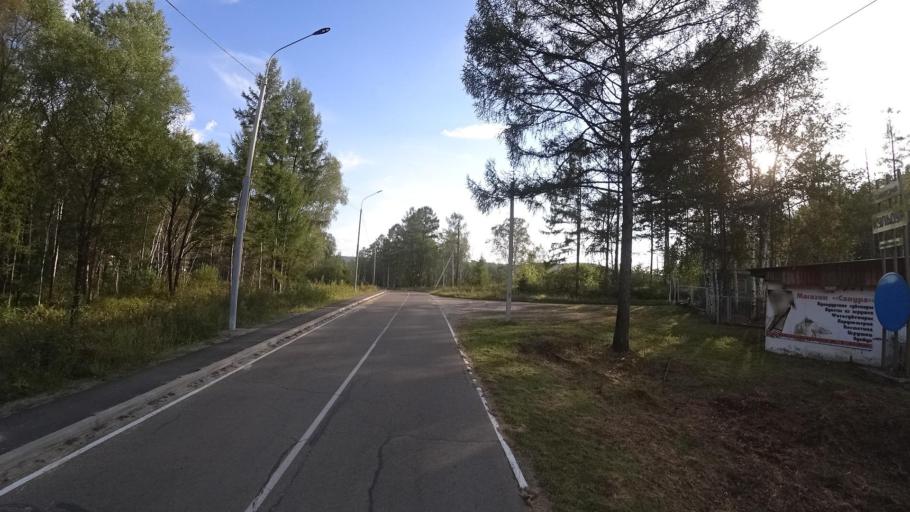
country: RU
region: Jewish Autonomous Oblast
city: Kul'dur
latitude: 49.2058
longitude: 131.6210
